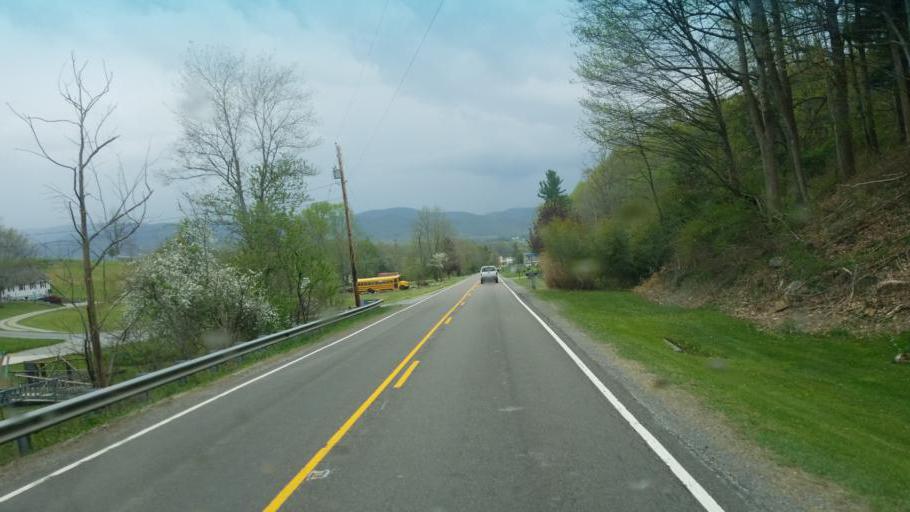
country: US
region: Virginia
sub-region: Smyth County
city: Atkins
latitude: 36.7970
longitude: -81.4023
